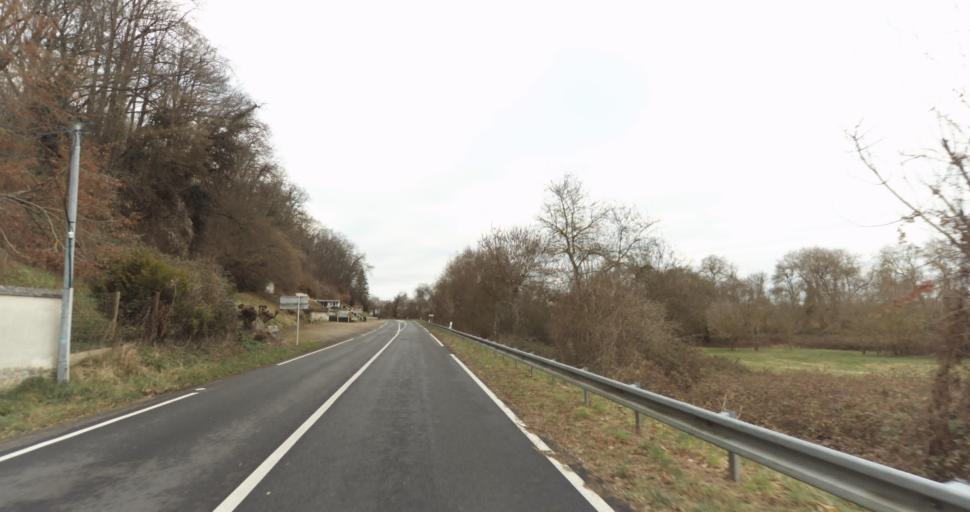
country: FR
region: Pays de la Loire
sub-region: Departement de Maine-et-Loire
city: Saumur
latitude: 47.2815
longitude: -0.1216
